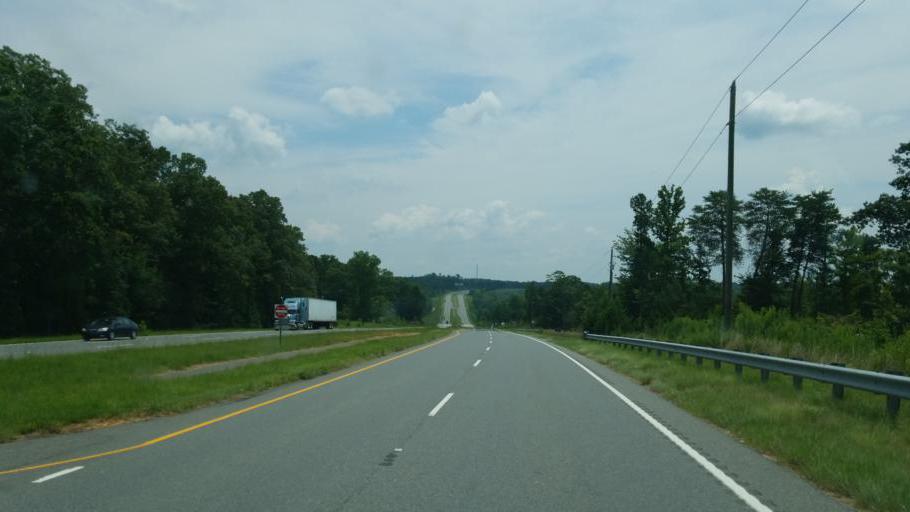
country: US
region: South Carolina
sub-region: Cherokee County
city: Blacksburg
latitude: 35.0615
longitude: -81.3946
